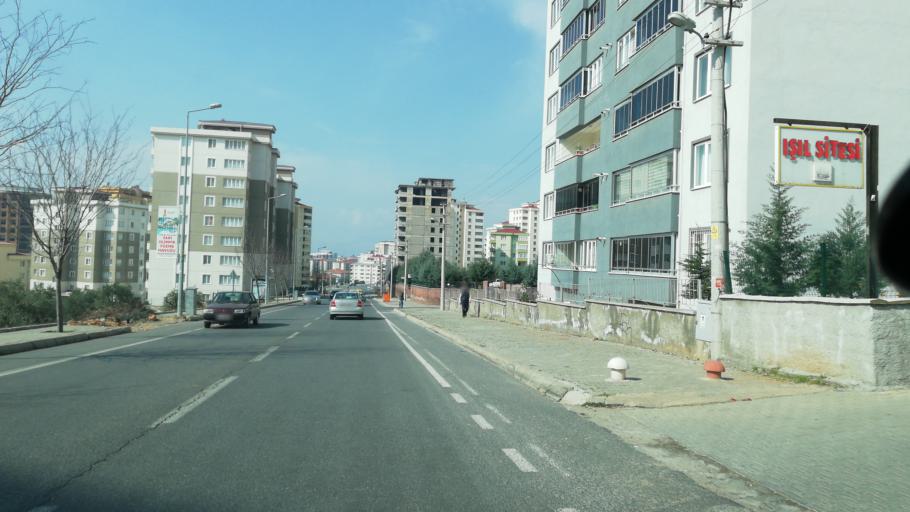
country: TR
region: Kahramanmaras
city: Kahramanmaras
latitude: 37.5866
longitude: 36.8732
